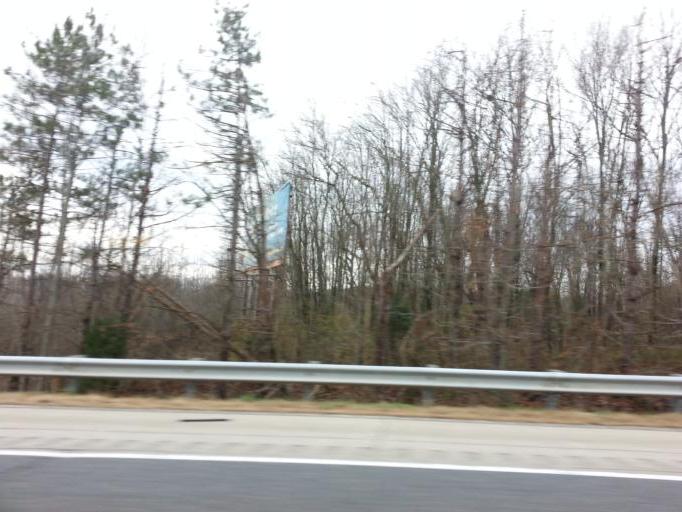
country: US
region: Indiana
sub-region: Ripley County
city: Batesville
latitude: 39.3120
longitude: -85.2237
